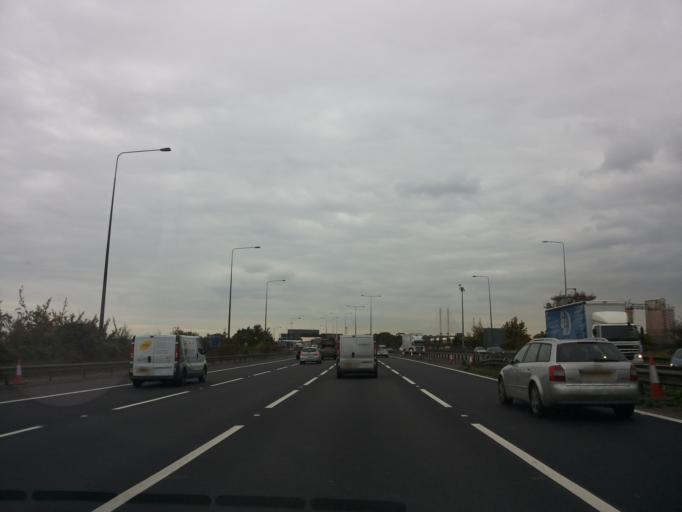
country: GB
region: England
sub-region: Kent
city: West Thurrock
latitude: 51.4814
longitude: 0.2668
